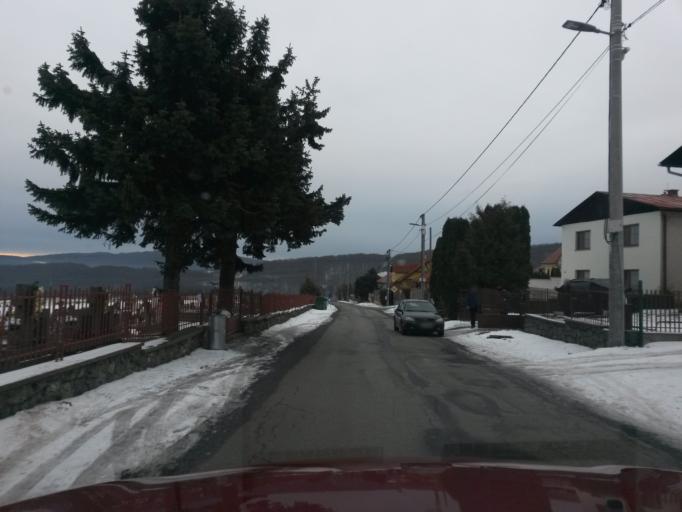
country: SK
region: Kosicky
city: Kosice
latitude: 48.7425
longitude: 21.1226
